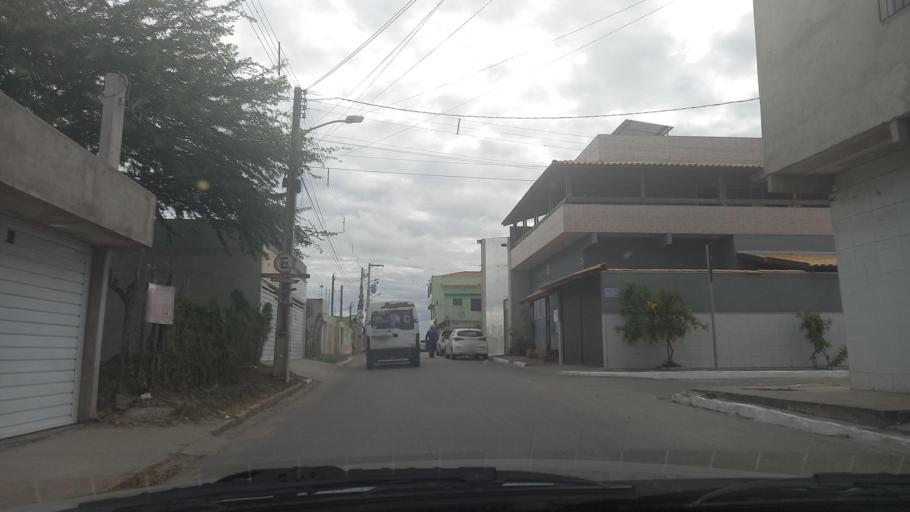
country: BR
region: Pernambuco
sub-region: Caruaru
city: Caruaru
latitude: -8.2894
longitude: -36.0280
